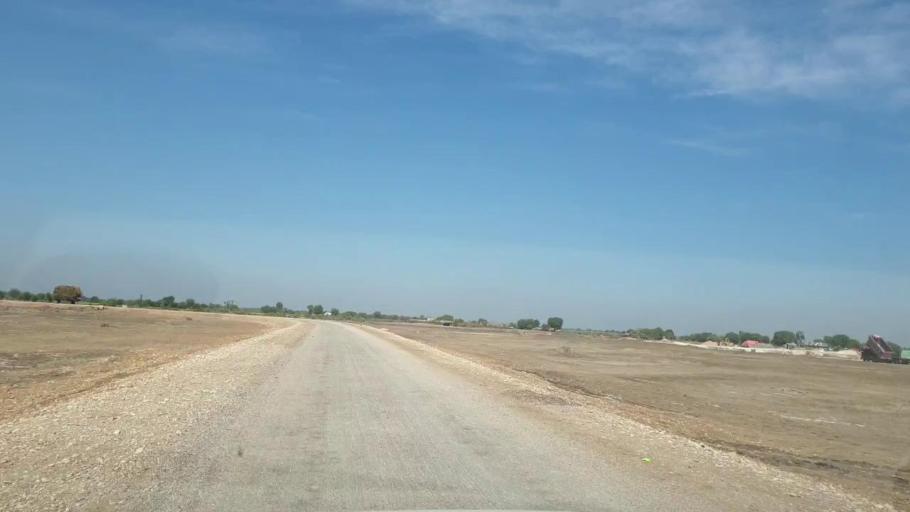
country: PK
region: Sindh
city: Mirpur Khas
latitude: 25.6482
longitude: 69.1917
